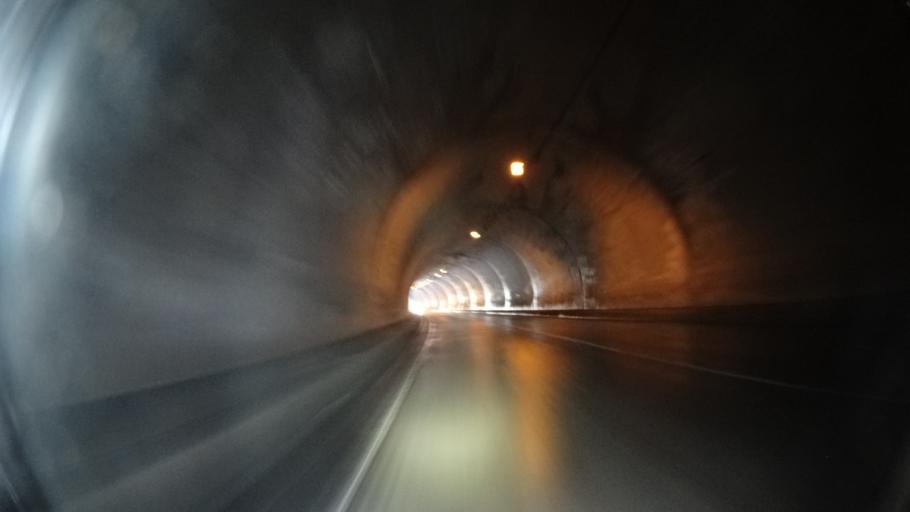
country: JP
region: Gunma
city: Tomioka
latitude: 36.0846
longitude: 138.7395
